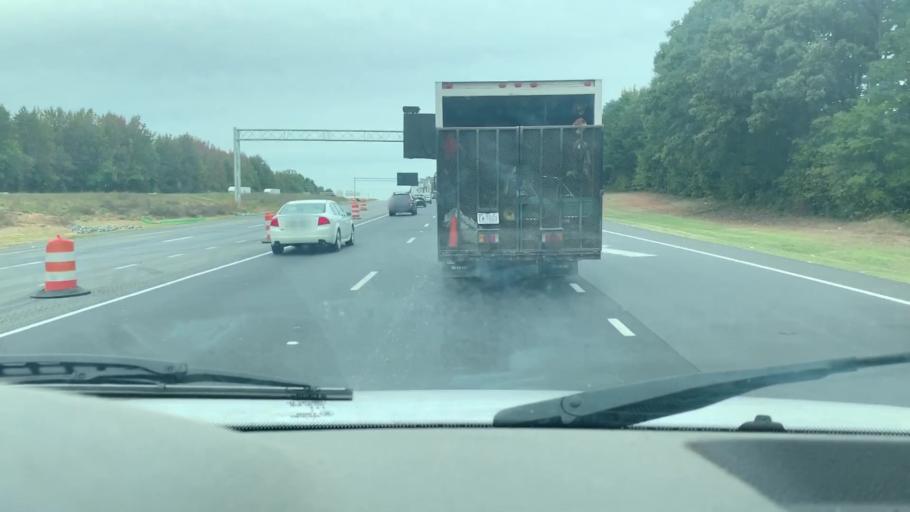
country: US
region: North Carolina
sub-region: Mecklenburg County
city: Cornelius
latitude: 35.4493
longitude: -80.8693
